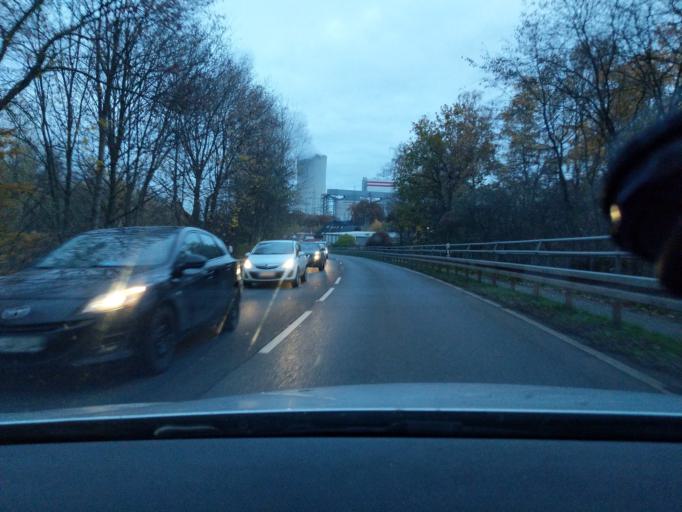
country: DE
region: North Rhine-Westphalia
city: Waltrop
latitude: 51.6209
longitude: 7.4505
